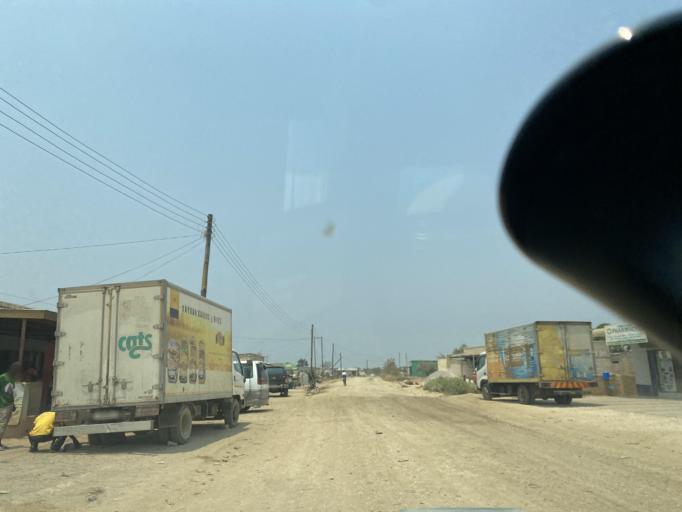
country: ZM
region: Lusaka
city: Lusaka
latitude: -15.5422
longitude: 28.3528
